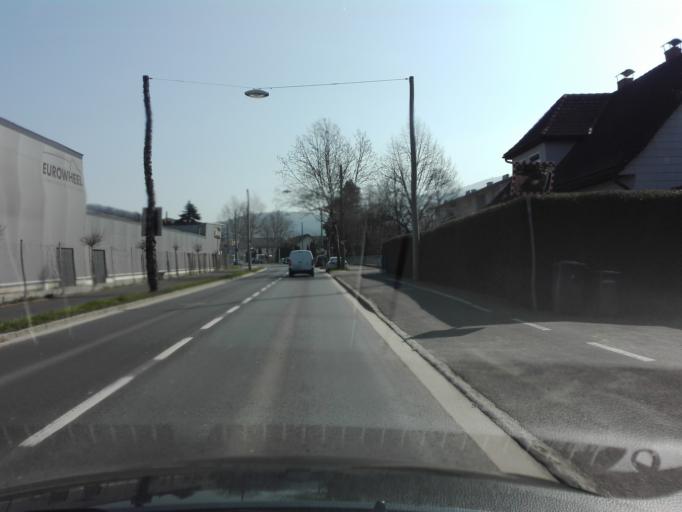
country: AT
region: Upper Austria
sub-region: Linz Stadt
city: Linz
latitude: 48.3280
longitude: 14.3265
